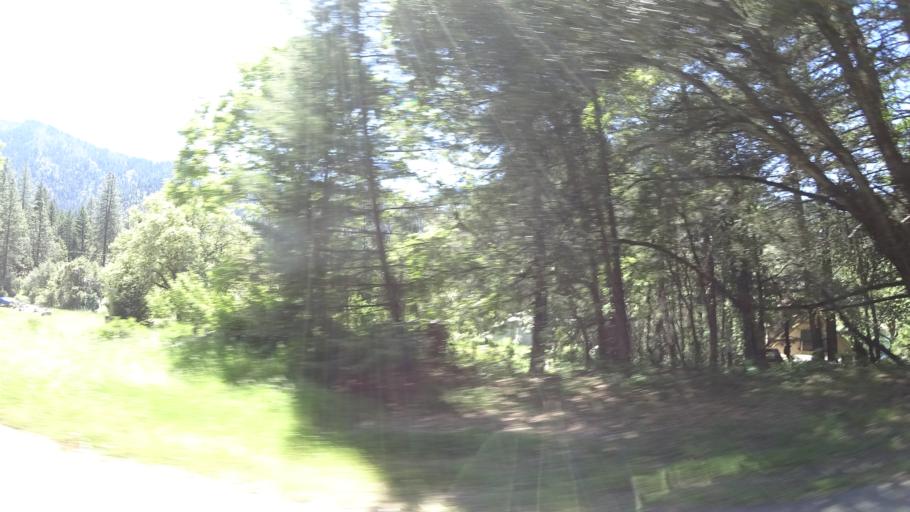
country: US
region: California
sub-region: Trinity County
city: Hayfork
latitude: 40.7814
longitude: -123.3334
